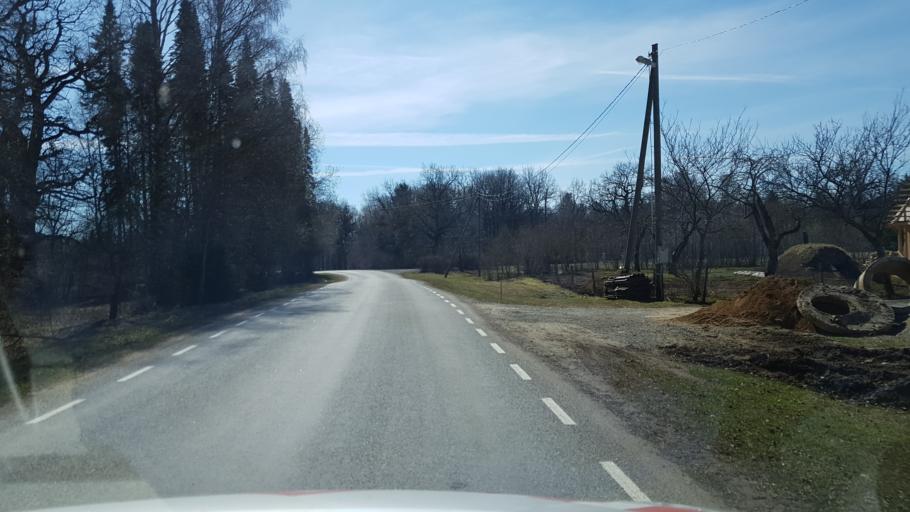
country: EE
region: Laeaene-Virumaa
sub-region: Vinni vald
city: Vinni
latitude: 59.2889
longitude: 26.4268
